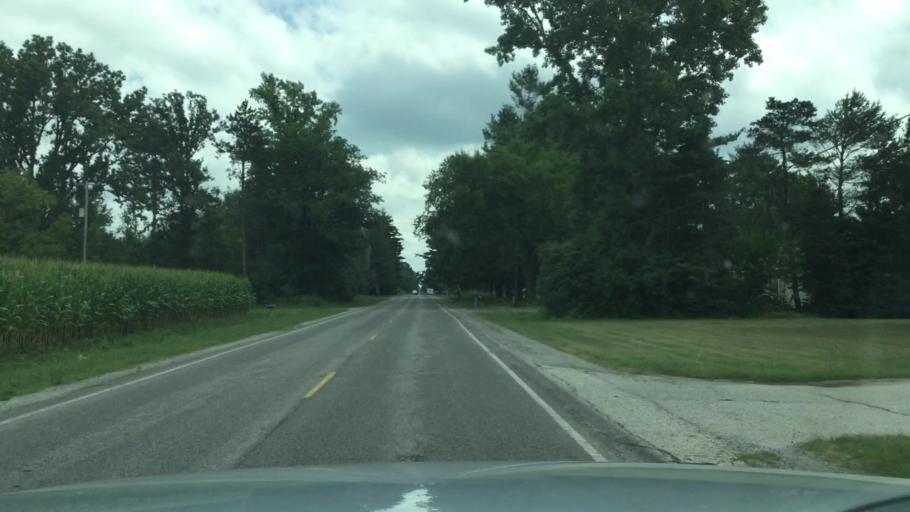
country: US
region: Michigan
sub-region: Saginaw County
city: Birch Run
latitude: 43.2934
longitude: -83.8107
